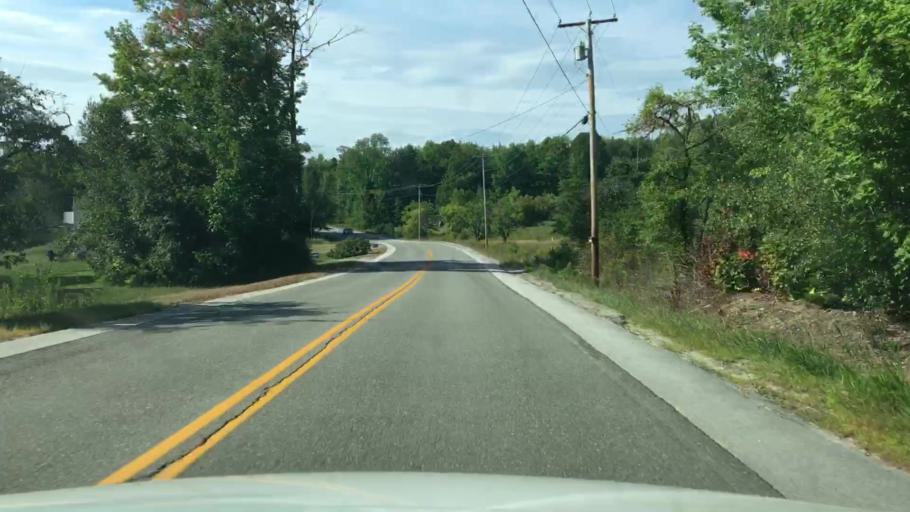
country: US
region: Maine
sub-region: Penobscot County
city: Enfield
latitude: 45.2130
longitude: -68.5256
